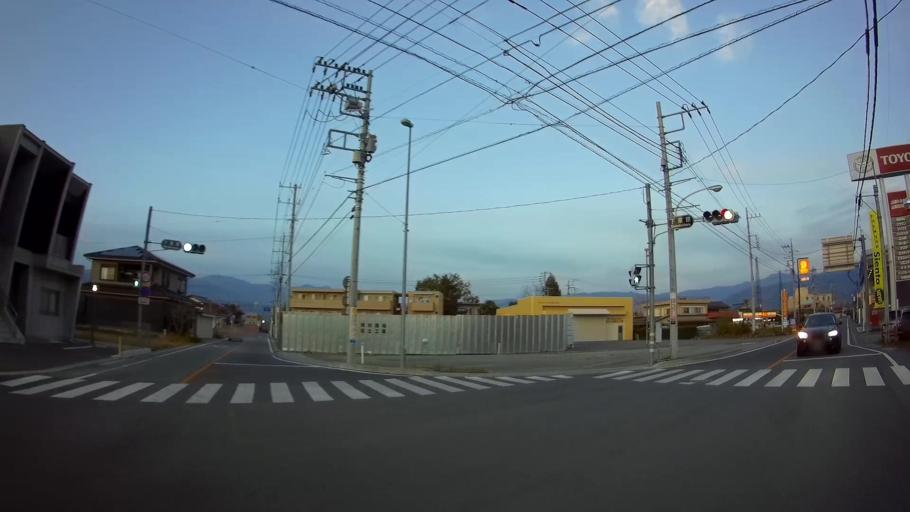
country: JP
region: Yamanashi
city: Enzan
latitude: 35.6639
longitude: 138.6924
